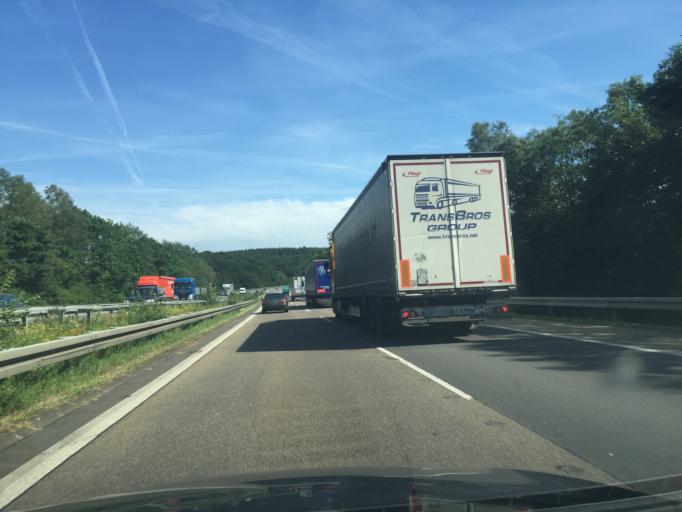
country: DE
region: North Rhine-Westphalia
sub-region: Regierungsbezirk Arnsberg
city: Drolshagen
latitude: 51.0501
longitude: 7.7865
